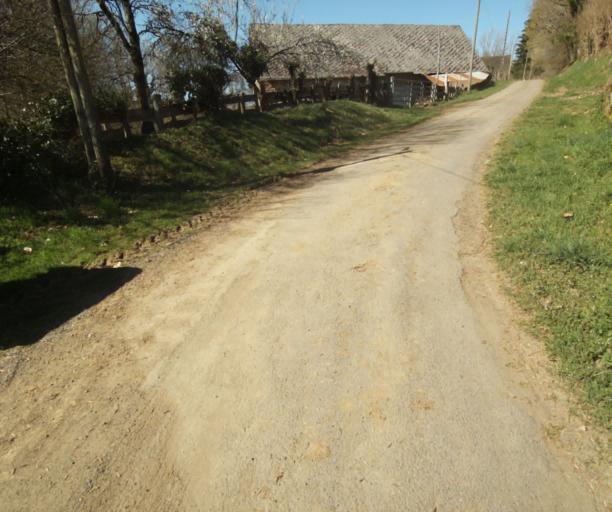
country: FR
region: Limousin
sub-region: Departement de la Correze
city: Saint-Clement
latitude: 45.3926
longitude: 1.6605
